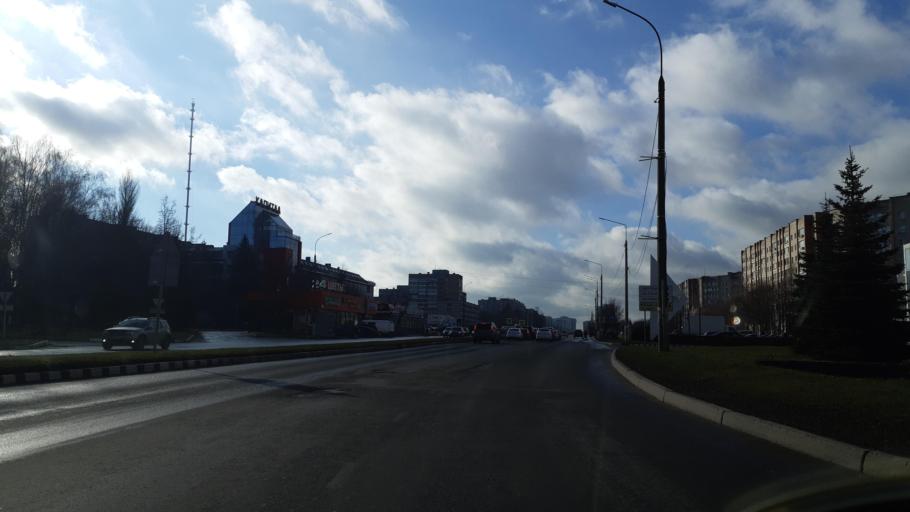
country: RU
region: Kaluga
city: Obninsk
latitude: 55.1203
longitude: 36.6034
